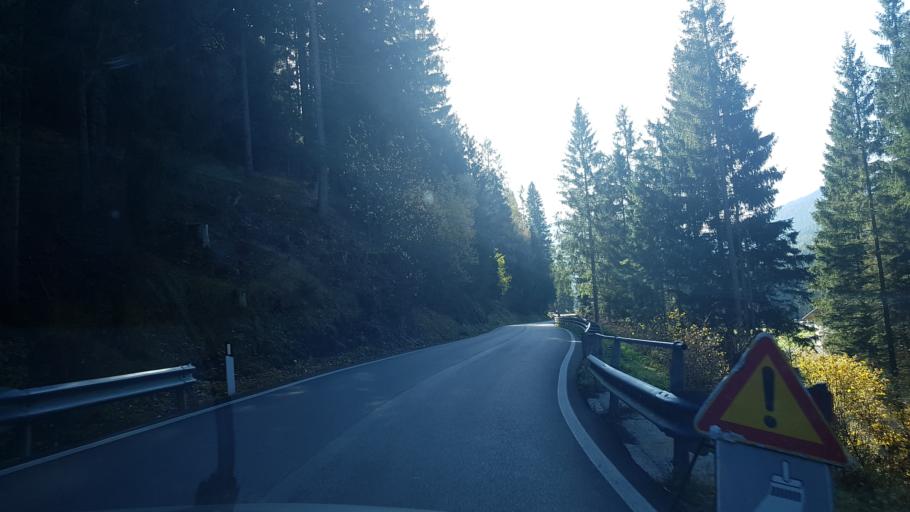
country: IT
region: Veneto
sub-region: Provincia di Belluno
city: Candide
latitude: 46.6205
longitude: 12.4737
